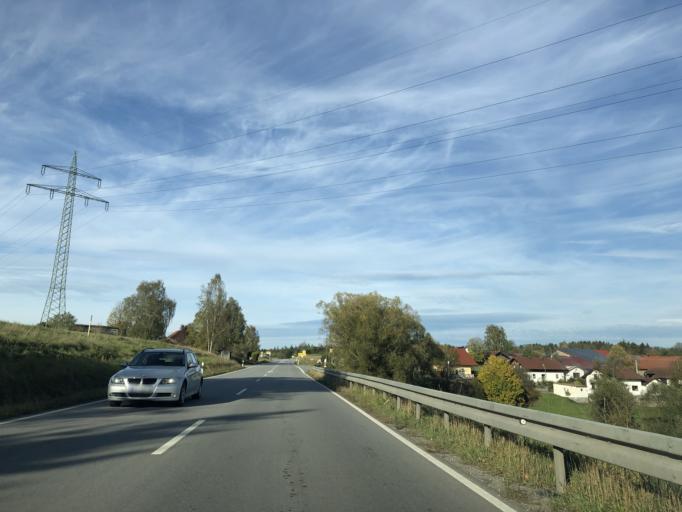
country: DE
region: Bavaria
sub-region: Lower Bavaria
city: Patersdorf
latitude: 49.0012
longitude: 12.9806
